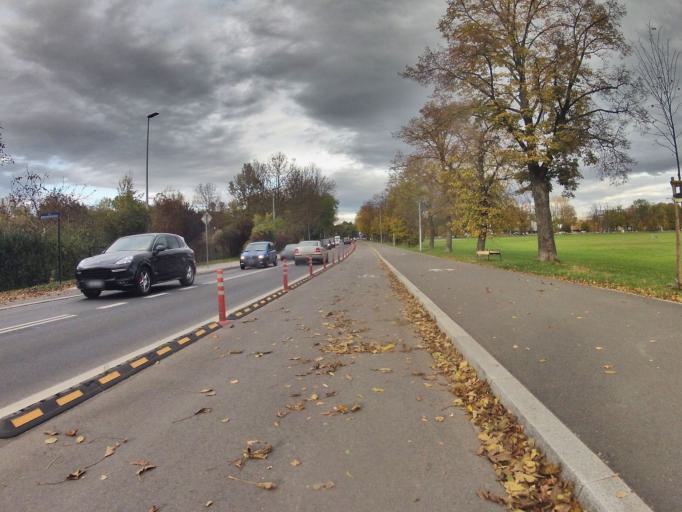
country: PL
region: Lesser Poland Voivodeship
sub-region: Krakow
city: Krakow
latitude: 50.0608
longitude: 19.9013
